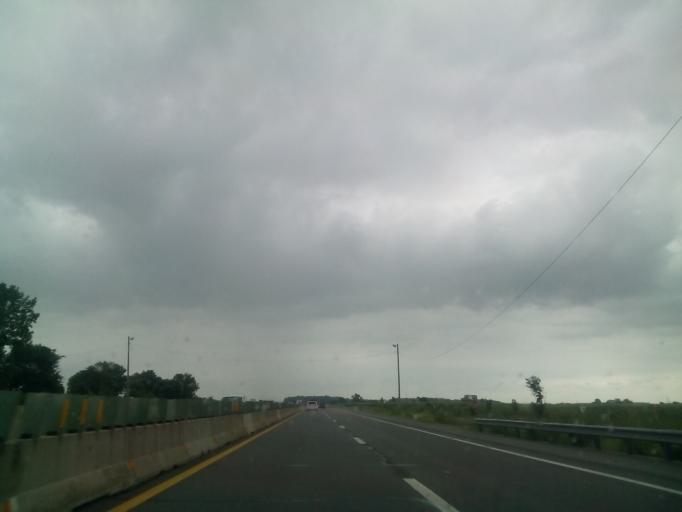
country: US
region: Ohio
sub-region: Sandusky County
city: Clyde
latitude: 41.3652
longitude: -82.9467
